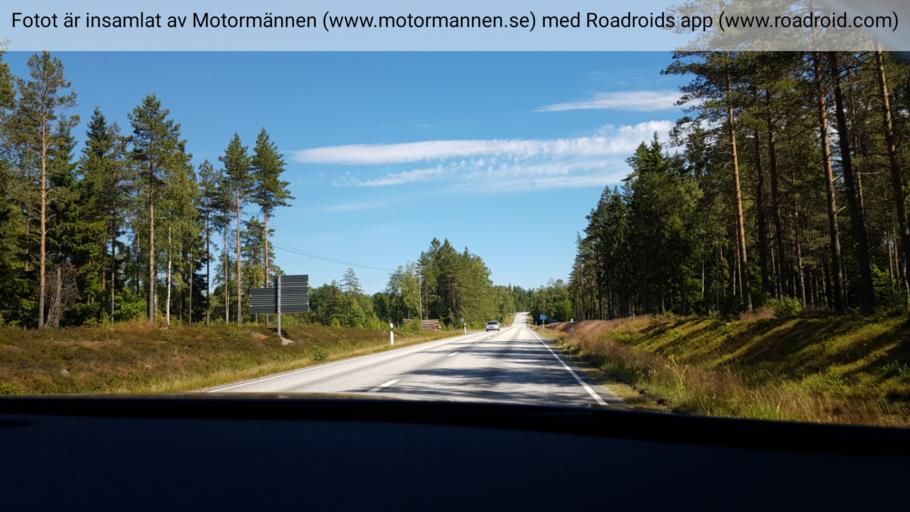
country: SE
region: Joenkoeping
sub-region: Gnosjo Kommun
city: Gnosjoe
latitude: 57.3842
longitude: 13.7069
